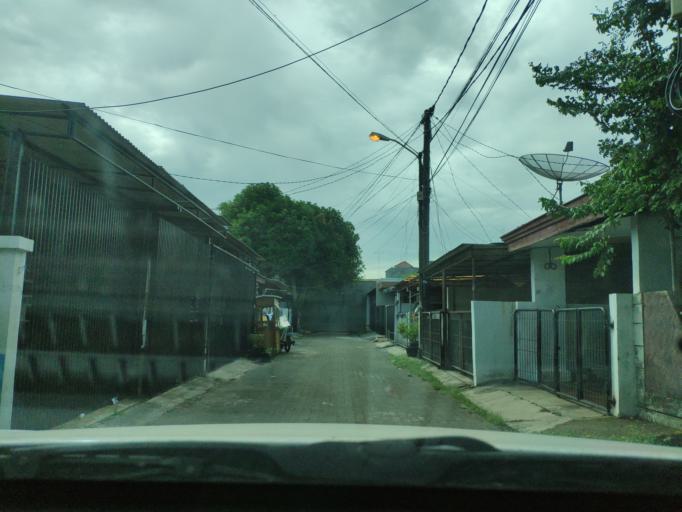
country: ID
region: West Java
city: Ciputat
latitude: -6.2232
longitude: 106.7111
